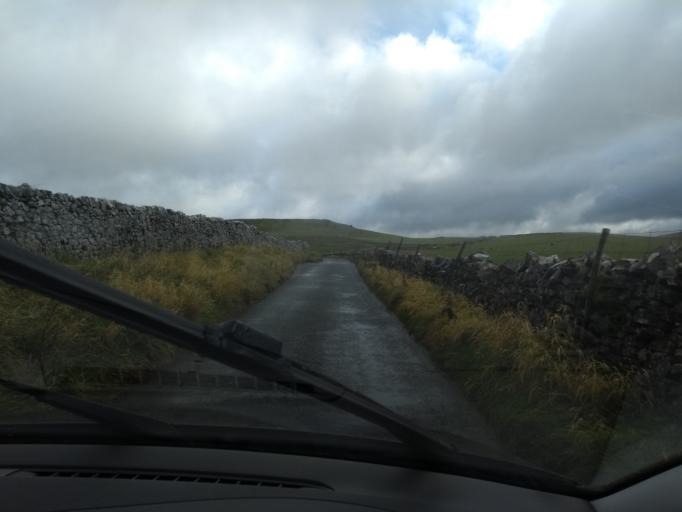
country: GB
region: England
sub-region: North Yorkshire
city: Settle
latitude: 54.1003
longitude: -2.2164
